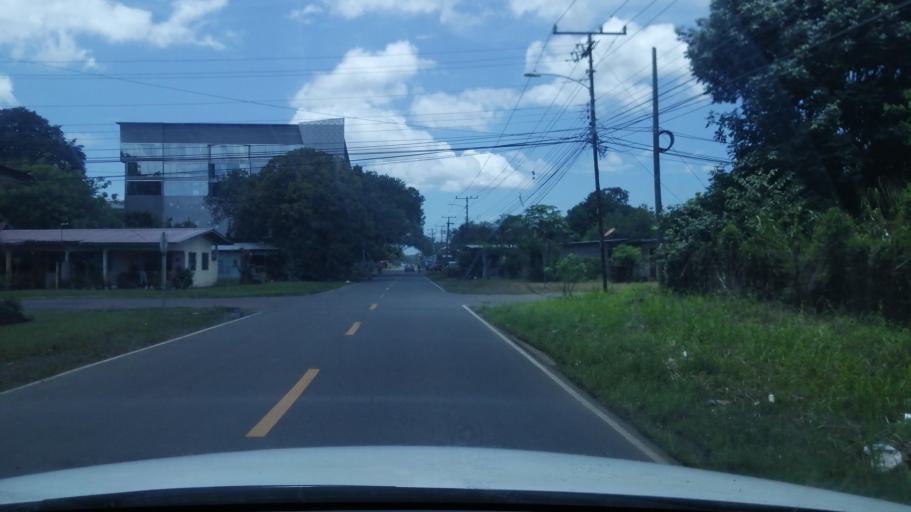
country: PA
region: Chiriqui
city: David
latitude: 8.4328
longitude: -82.4317
